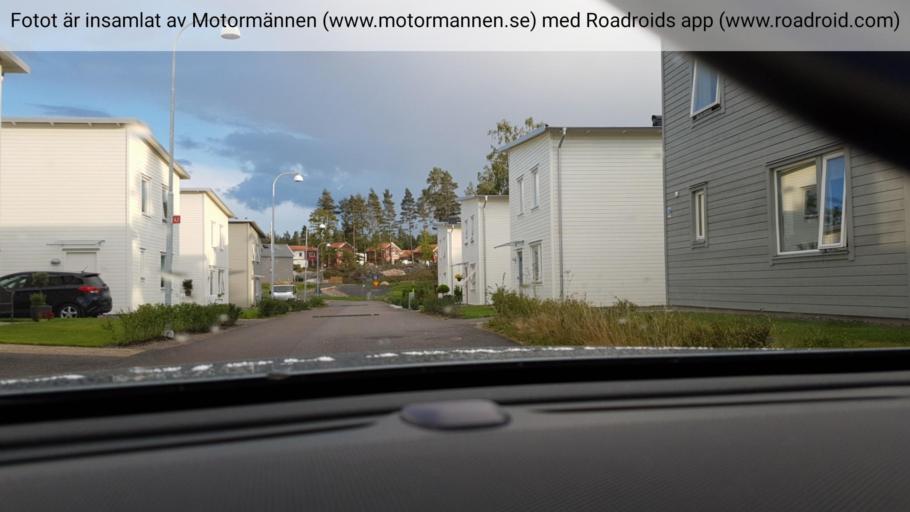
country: SE
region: Vaestra Goetaland
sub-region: Ale Kommun
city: Alvangen
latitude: 57.9504
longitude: 12.1250
